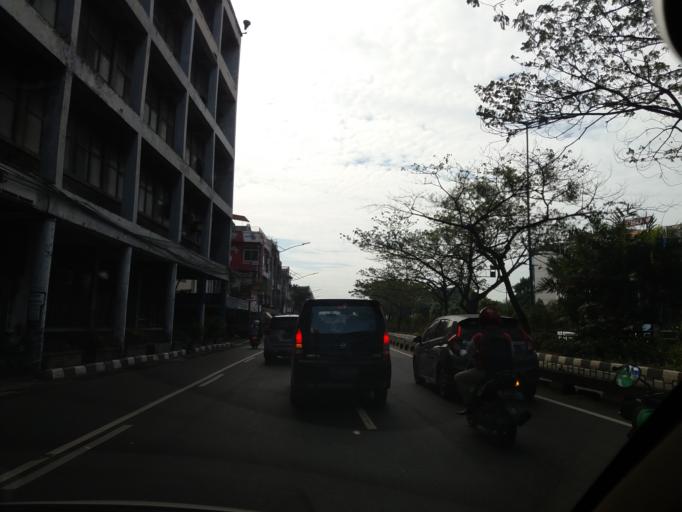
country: ID
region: Jakarta Raya
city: Jakarta
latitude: -6.1828
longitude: 106.8429
